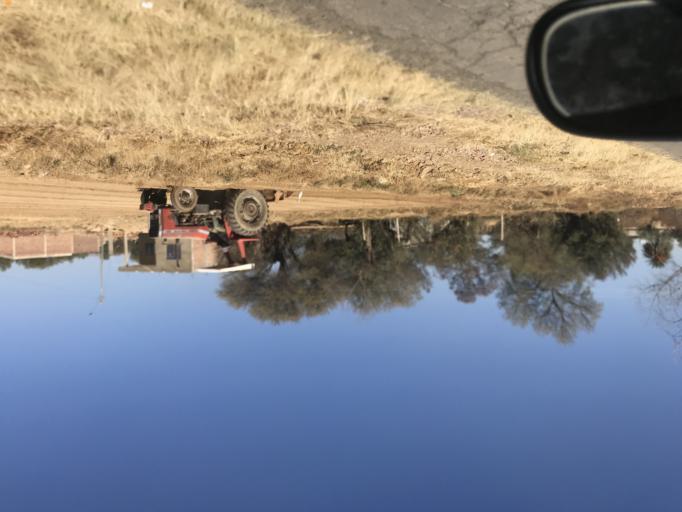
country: BO
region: Cochabamba
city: Cliza
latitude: -17.5974
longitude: -65.9550
